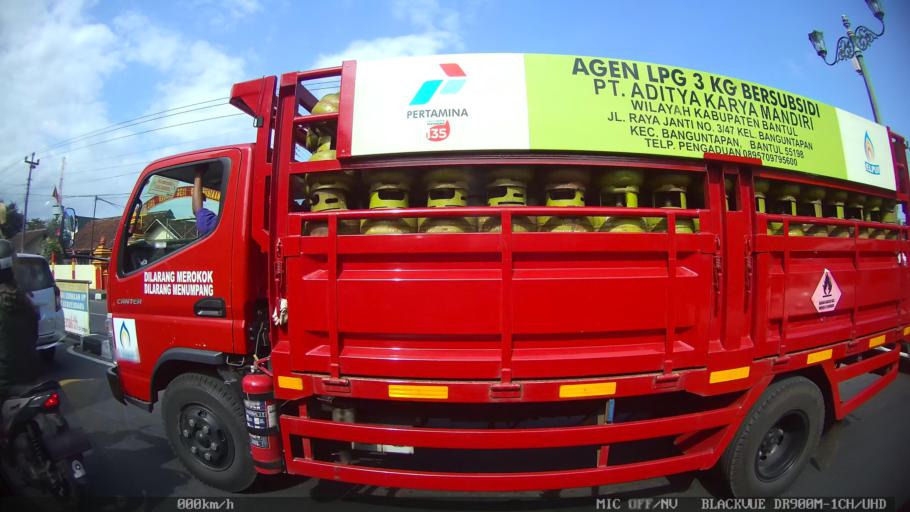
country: ID
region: Daerah Istimewa Yogyakarta
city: Sewon
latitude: -7.8373
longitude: 110.3921
